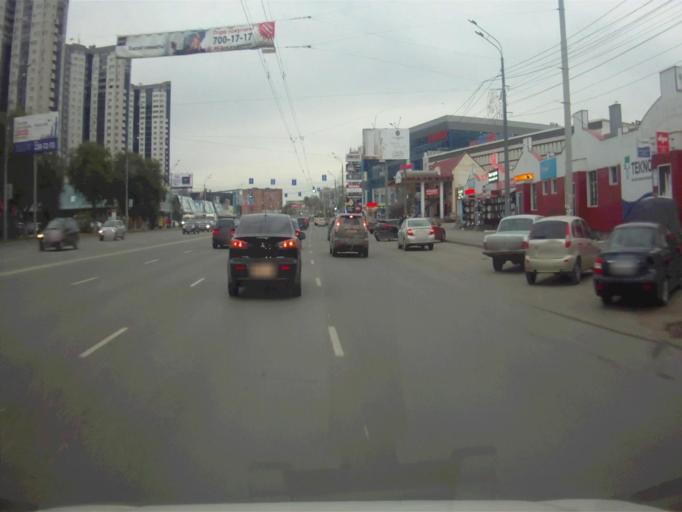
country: RU
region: Chelyabinsk
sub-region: Gorod Chelyabinsk
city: Chelyabinsk
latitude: 55.1702
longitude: 61.3725
